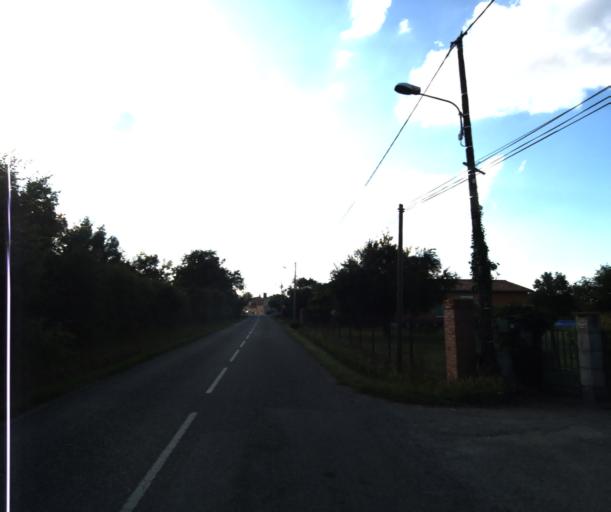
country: FR
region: Midi-Pyrenees
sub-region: Departement de la Haute-Garonne
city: Labastidette
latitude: 43.4814
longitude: 1.2473
